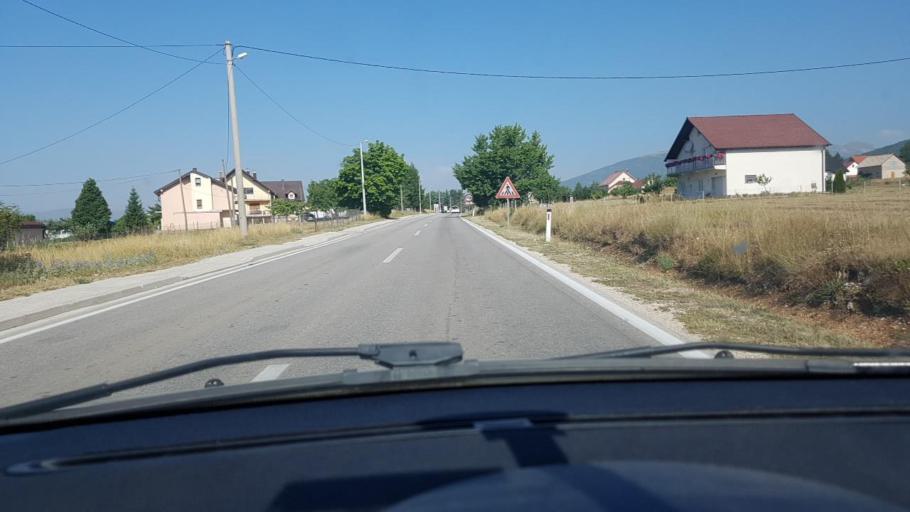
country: BA
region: Federation of Bosnia and Herzegovina
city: Livno
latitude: 43.8442
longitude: 16.9647
